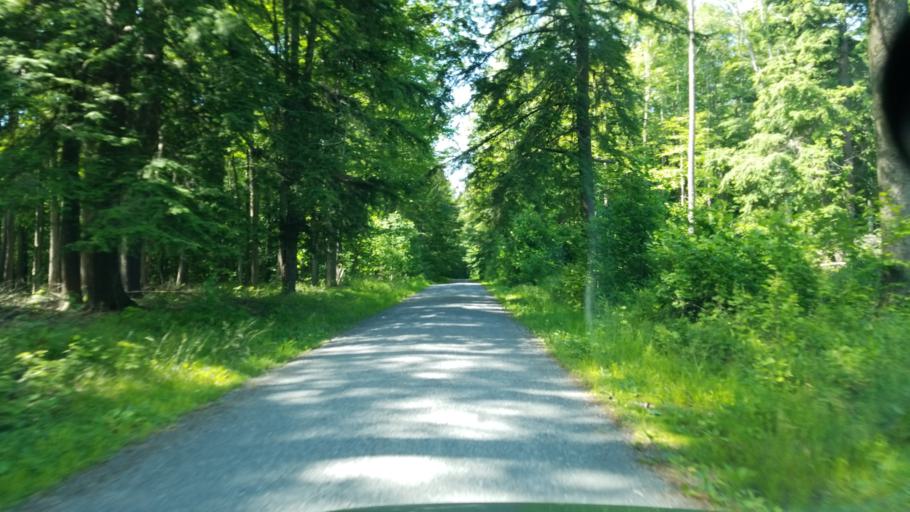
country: US
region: Pennsylvania
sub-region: Clearfield County
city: Clearfield
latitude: 41.1994
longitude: -78.4833
